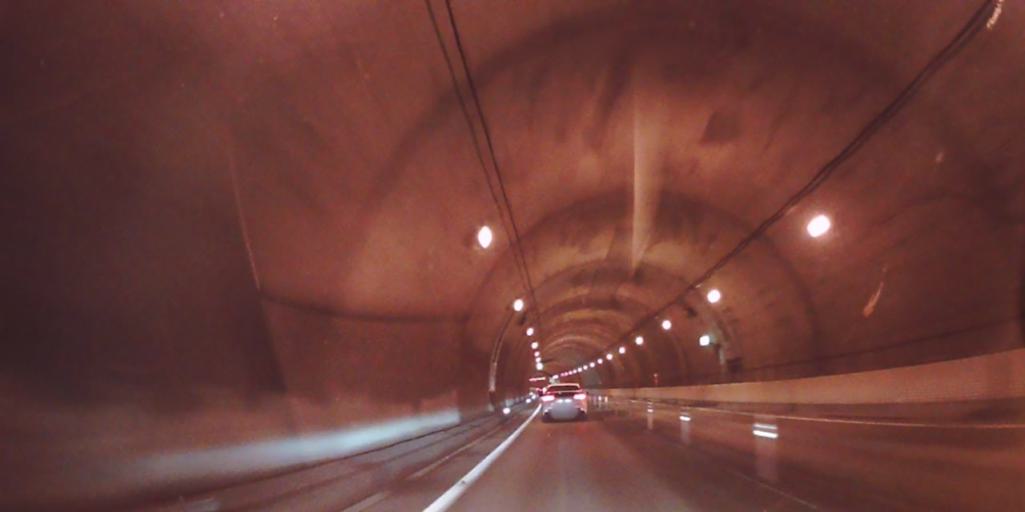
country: JP
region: Hokkaido
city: Date
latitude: 42.5549
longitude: 140.7830
